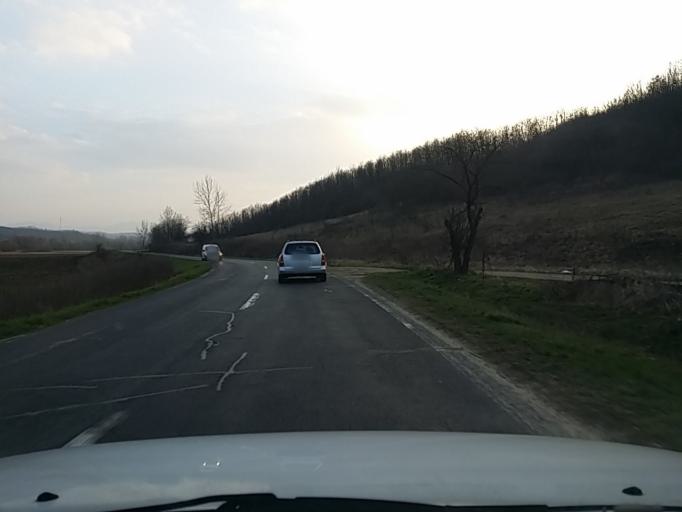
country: HU
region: Heves
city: Petervasara
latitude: 48.0417
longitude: 20.1281
